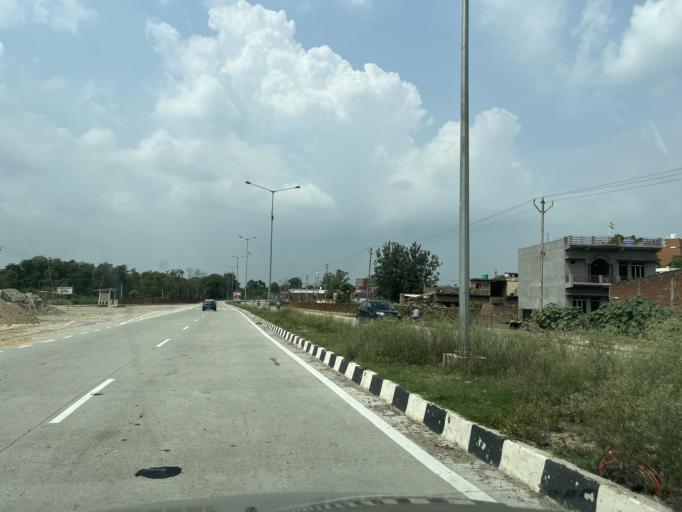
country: IN
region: Uttar Pradesh
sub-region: Bijnor
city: Sherkot
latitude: 29.3300
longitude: 78.5685
